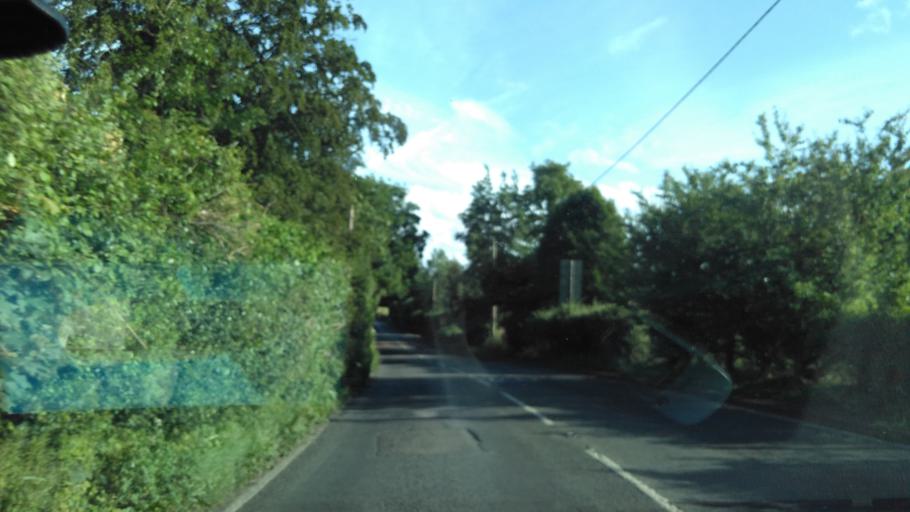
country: GB
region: England
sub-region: Kent
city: Faversham
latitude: 51.2733
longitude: 0.8806
